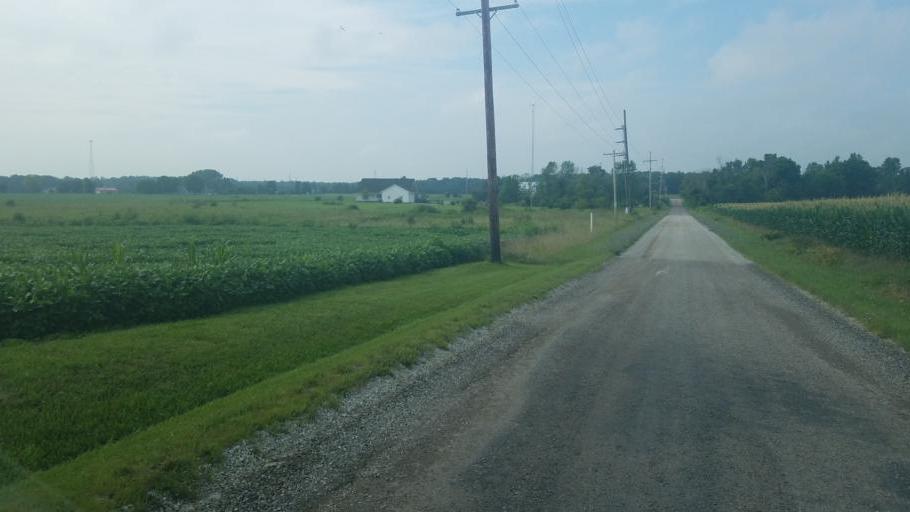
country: US
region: Ohio
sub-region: Delaware County
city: Ashley
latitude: 40.3713
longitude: -82.9114
